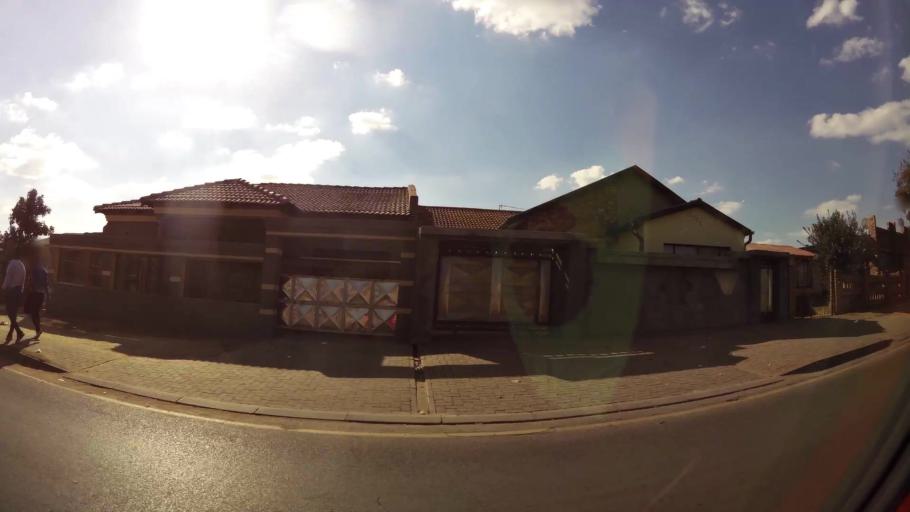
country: ZA
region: Gauteng
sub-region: City of Johannesburg Metropolitan Municipality
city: Roodepoort
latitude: -26.2143
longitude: 27.8815
